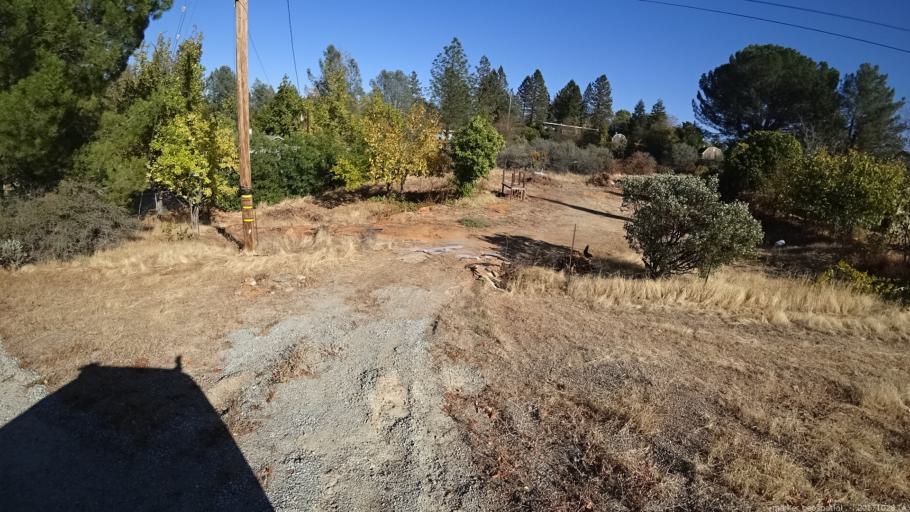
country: US
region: California
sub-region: Shasta County
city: Shasta
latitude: 40.6251
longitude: -122.4612
